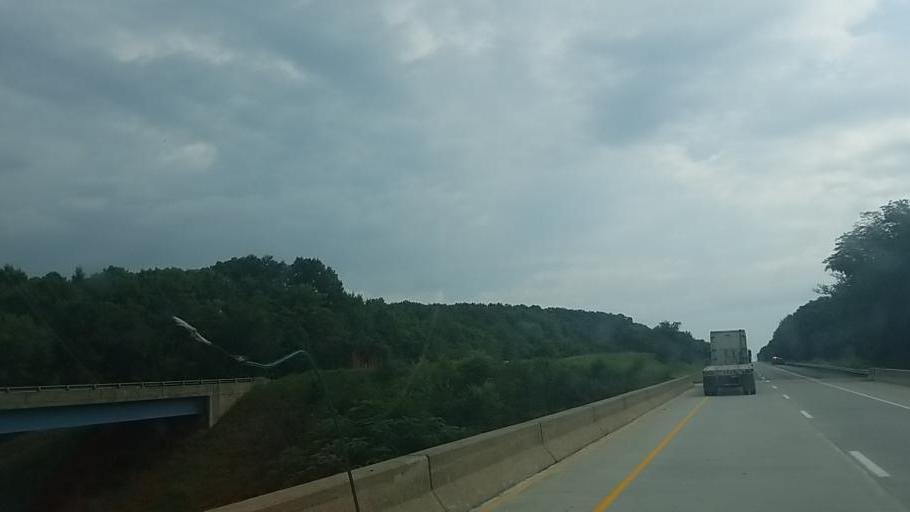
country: US
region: Pennsylvania
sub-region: Juniata County
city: Mifflintown
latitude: 40.5601
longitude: -77.2741
